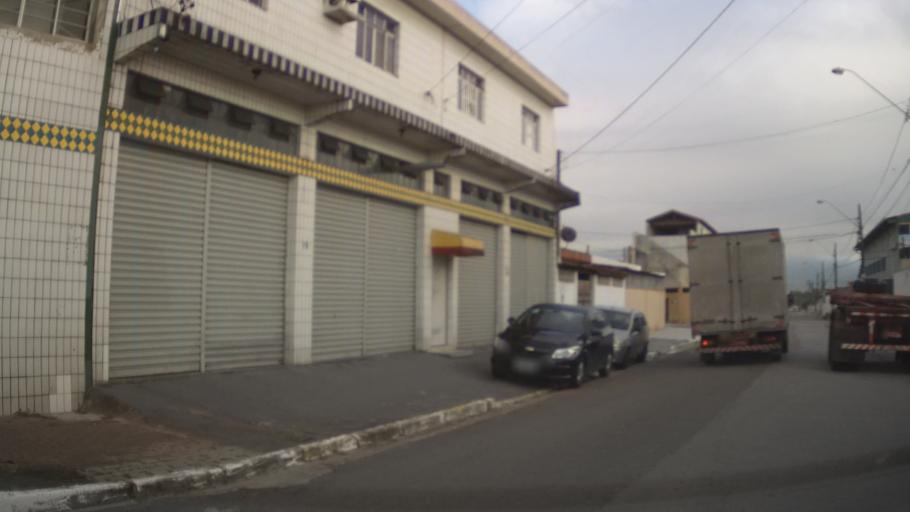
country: BR
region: Sao Paulo
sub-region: Praia Grande
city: Praia Grande
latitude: -24.0162
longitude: -46.4659
